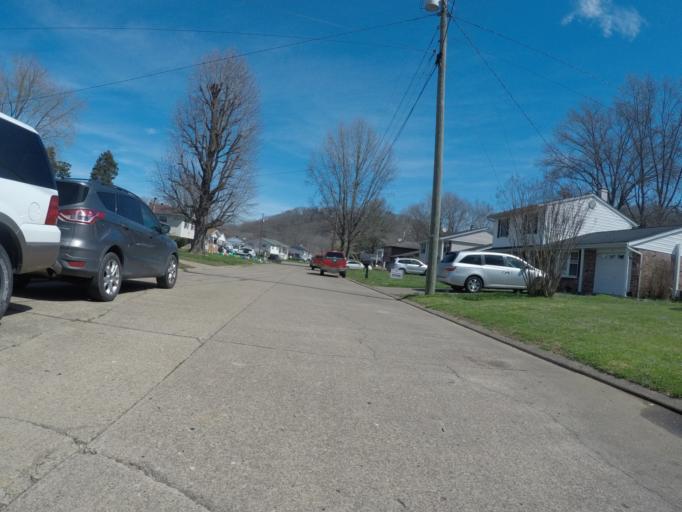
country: US
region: West Virginia
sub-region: Cabell County
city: Pea Ridge
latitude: 38.3976
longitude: -82.3162
